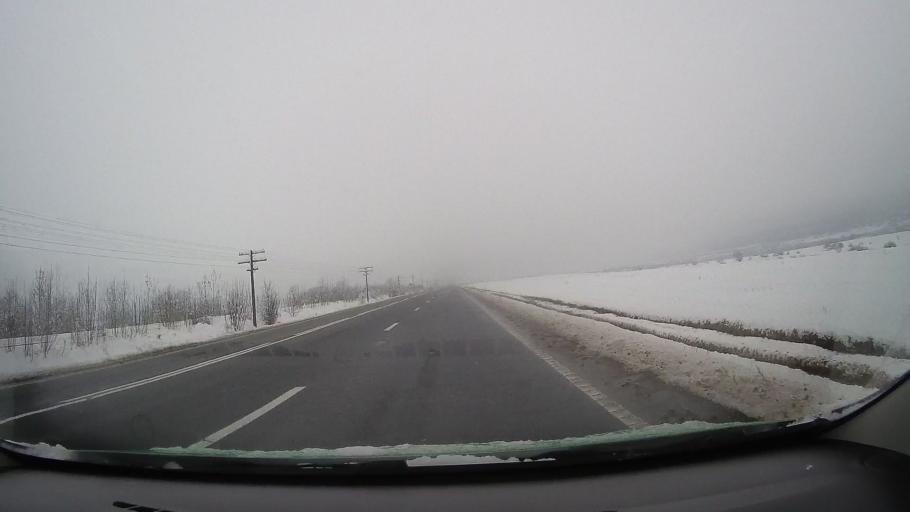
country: RO
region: Sibiu
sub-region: Oras Saliste
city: Saliste
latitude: 45.7953
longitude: 23.9120
